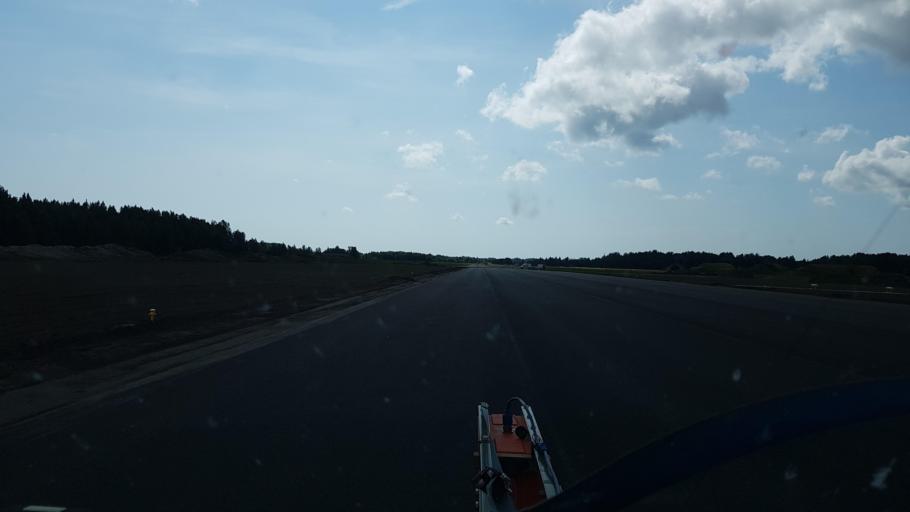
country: EE
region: Paernumaa
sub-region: Sauga vald
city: Sauga
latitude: 58.4164
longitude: 24.4699
